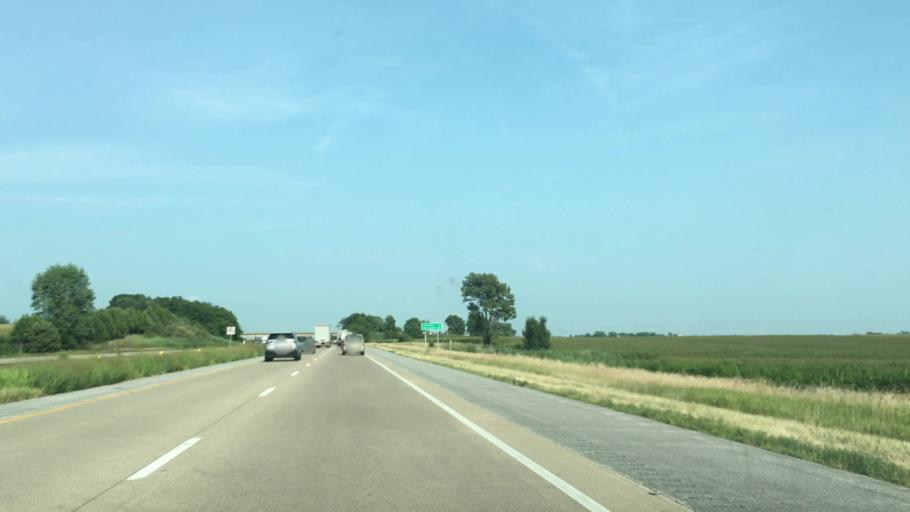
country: US
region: Iowa
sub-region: Cedar County
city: Durant
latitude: 41.6331
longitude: -90.9059
